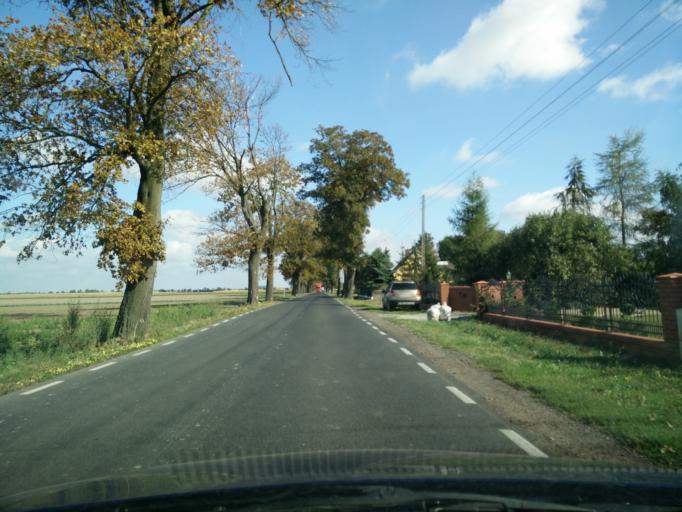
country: PL
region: Greater Poland Voivodeship
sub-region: Powiat sredzki
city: Sroda Wielkopolska
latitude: 52.2467
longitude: 17.2936
